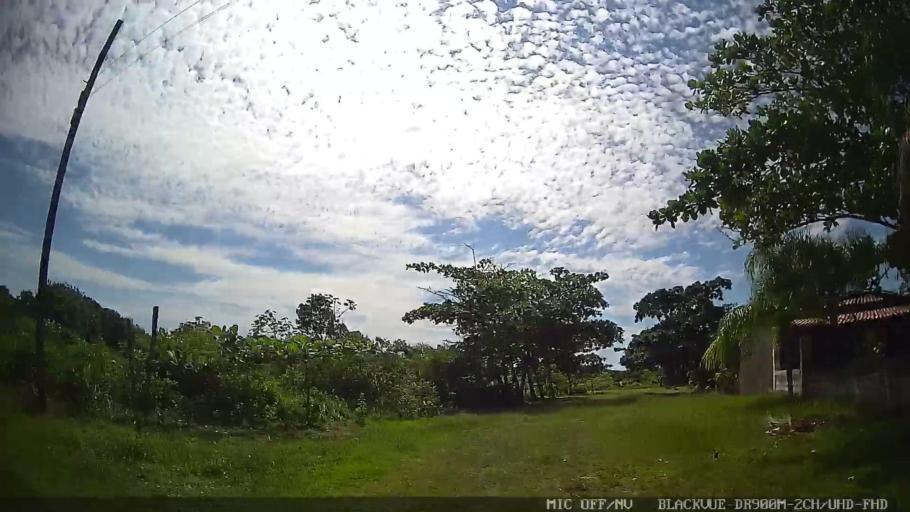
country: BR
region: Sao Paulo
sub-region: Iguape
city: Iguape
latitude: -24.7959
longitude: -47.6288
